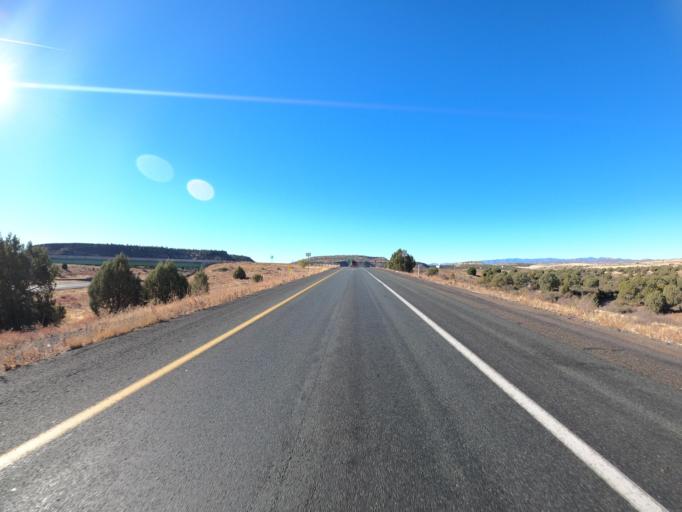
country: US
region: Arizona
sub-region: Yavapai County
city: Camp Verde
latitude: 34.5153
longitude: -111.9924
